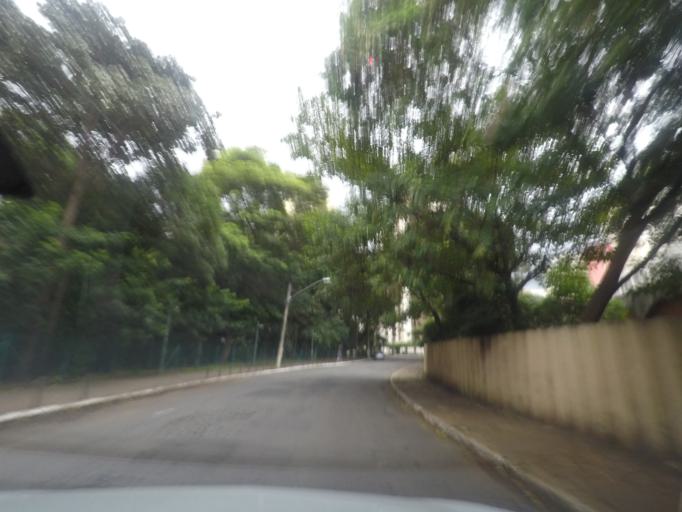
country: BR
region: Goias
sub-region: Goiania
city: Goiania
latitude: -16.6801
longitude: -49.2625
